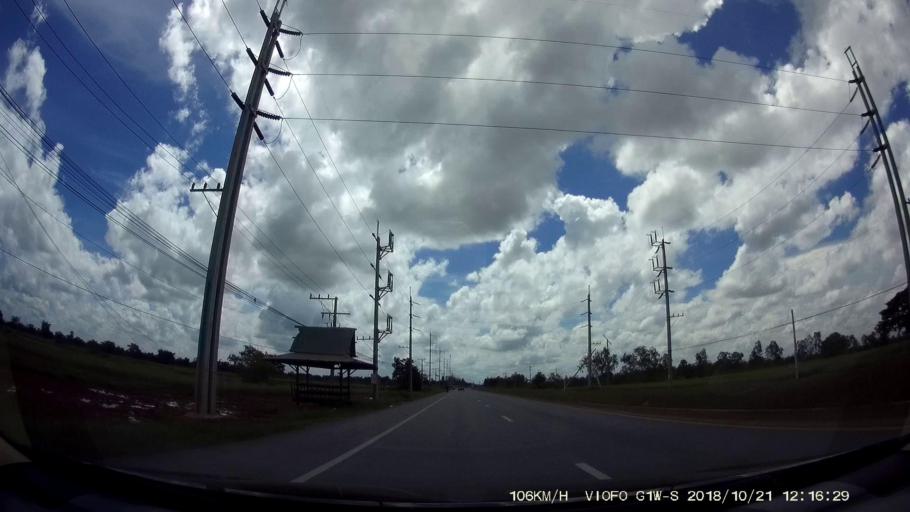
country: TH
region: Nakhon Ratchasima
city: Dan Khun Thot
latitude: 15.3468
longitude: 101.8256
